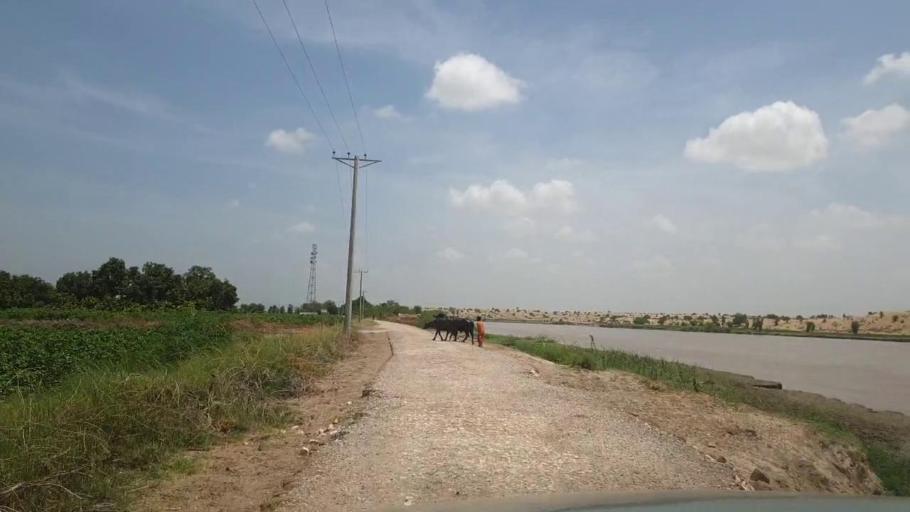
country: PK
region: Sindh
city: Kot Diji
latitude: 27.1439
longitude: 69.0144
